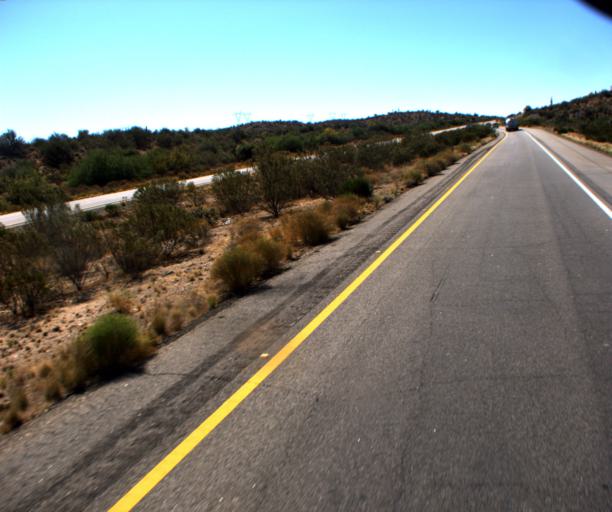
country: US
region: Arizona
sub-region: Yavapai County
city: Bagdad
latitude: 34.3637
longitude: -113.1753
